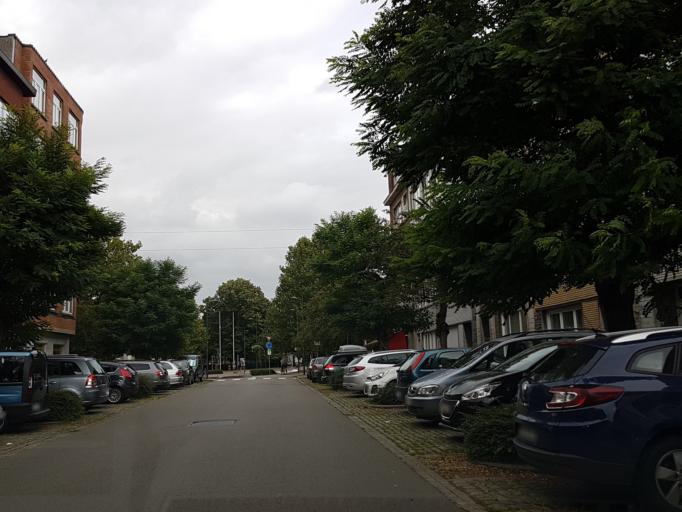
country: BE
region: Flanders
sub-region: Provincie Vlaams-Brabant
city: Diegem
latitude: 50.8716
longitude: 4.4024
